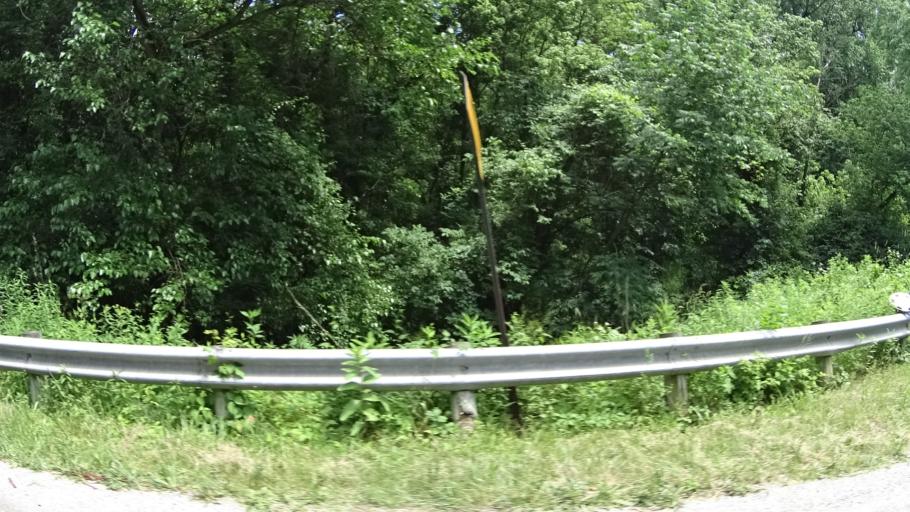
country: US
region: Ohio
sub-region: Erie County
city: Milan
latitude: 41.2929
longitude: -82.6142
